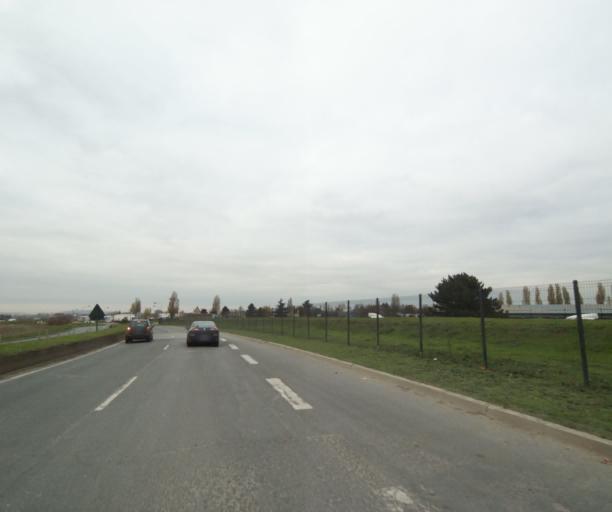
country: FR
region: Ile-de-France
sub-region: Departement du Val-d'Oise
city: Gonesse
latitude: 48.9761
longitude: 2.4586
